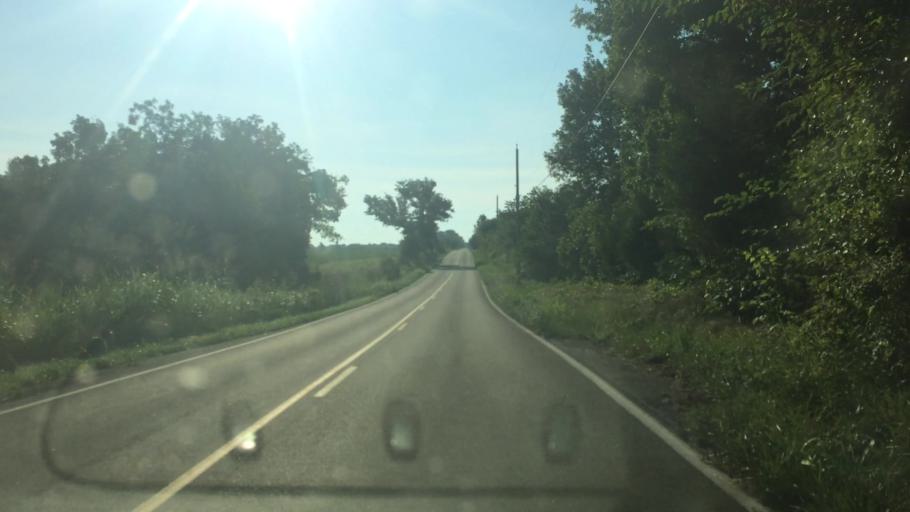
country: US
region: Missouri
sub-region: Greene County
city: Strafford
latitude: 37.2560
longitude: -93.1873
